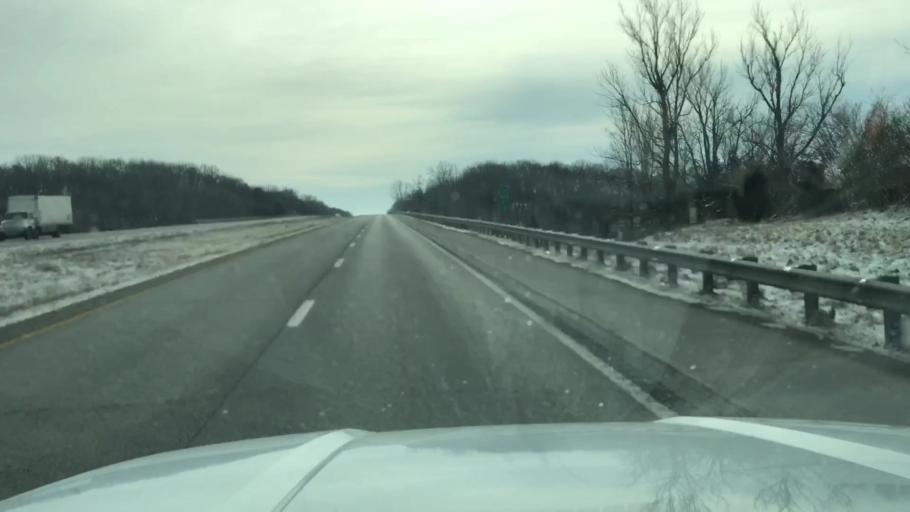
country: US
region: Missouri
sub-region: Andrew County
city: Savannah
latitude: 39.9329
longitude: -94.9271
